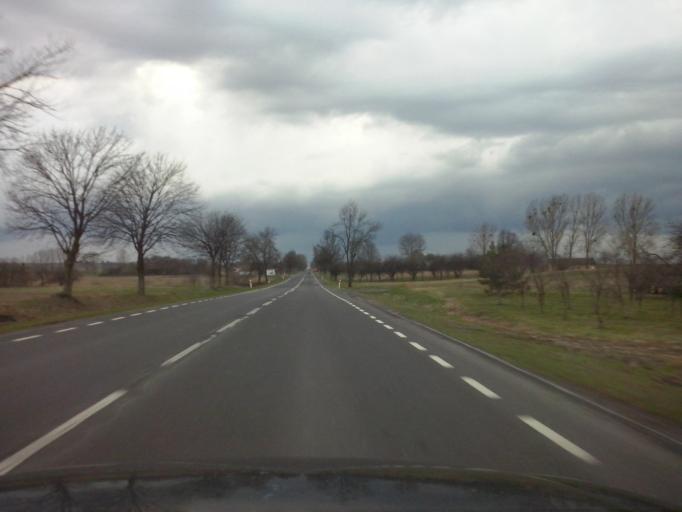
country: PL
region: Lublin Voivodeship
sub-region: Powiat chelmski
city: Rejowiec Fabryczny
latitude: 51.1716
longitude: 23.3006
